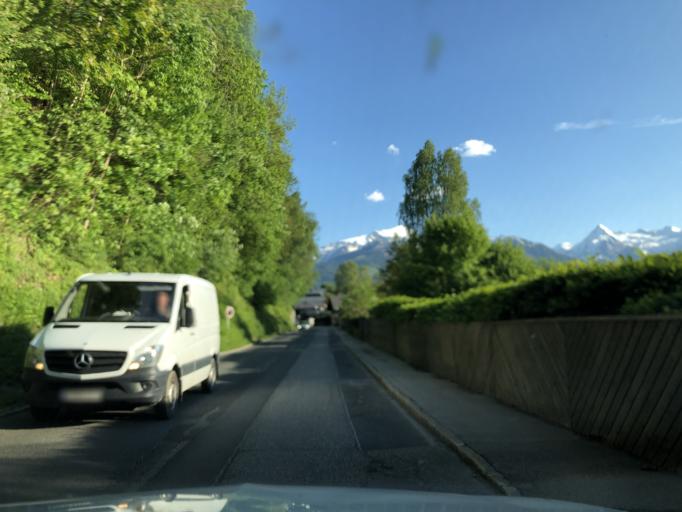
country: AT
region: Salzburg
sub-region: Politischer Bezirk Zell am See
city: Zell am See
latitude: 47.3175
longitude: 12.8155
